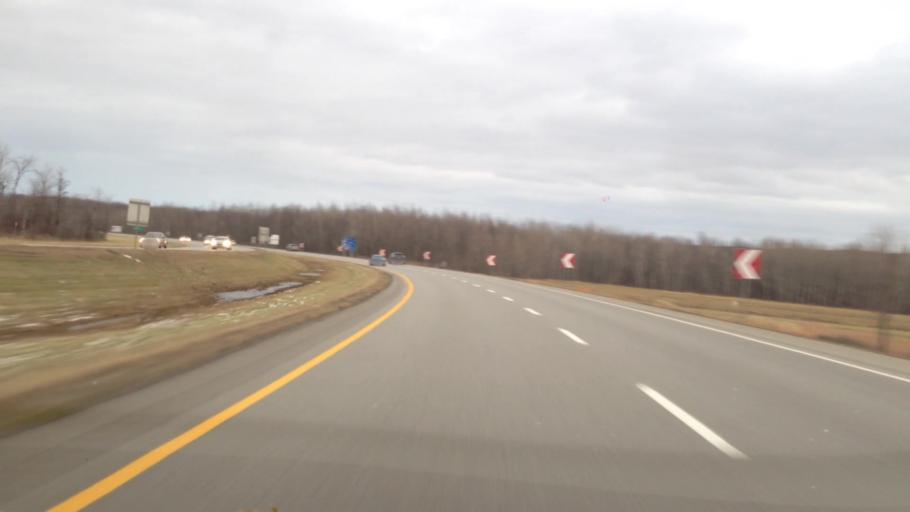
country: CA
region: Quebec
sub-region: Monteregie
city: Rigaud
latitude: 45.4864
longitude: -74.3421
